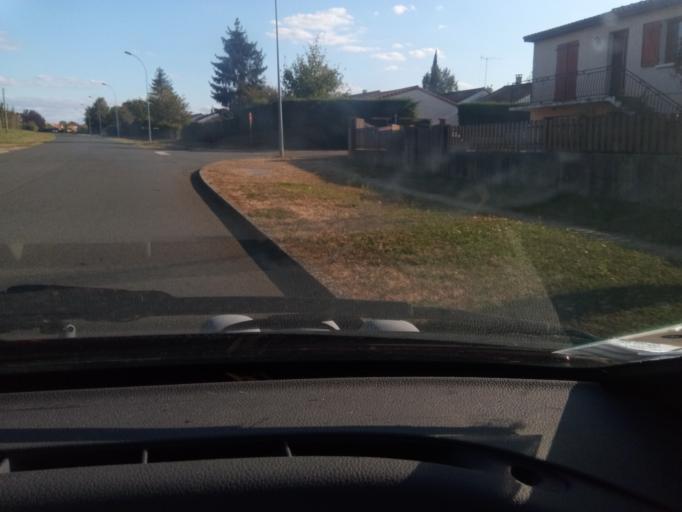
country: FR
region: Poitou-Charentes
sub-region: Departement de la Vienne
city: Lussac-les-Chateaux
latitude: 46.4019
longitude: 0.7155
